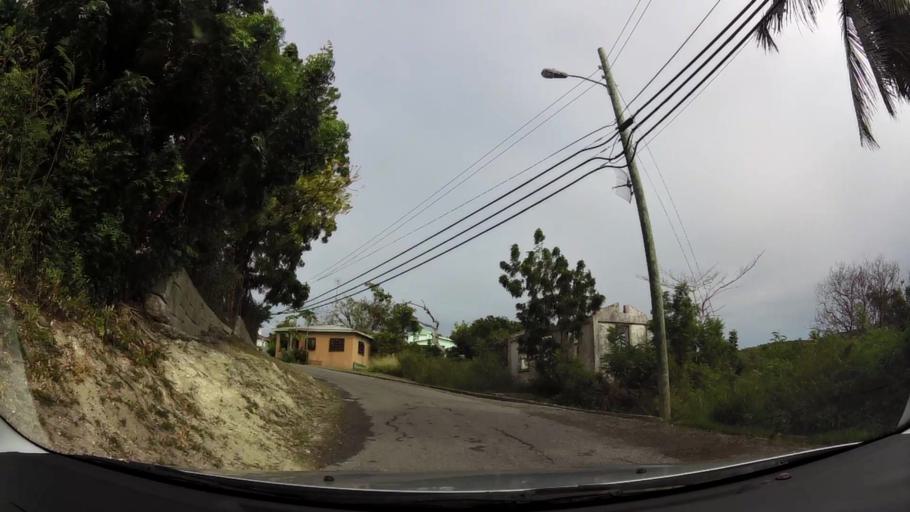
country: AG
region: Saint Peter
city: Parham
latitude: 17.0571
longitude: -61.7247
